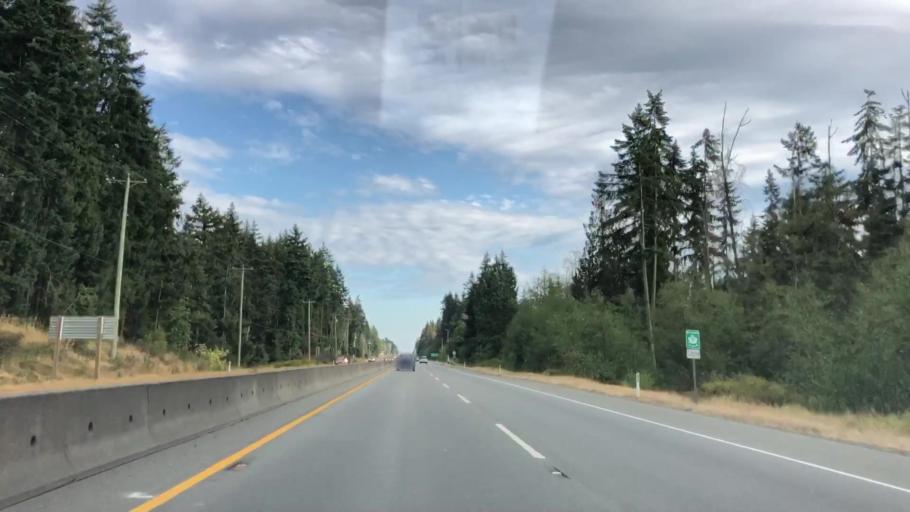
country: CA
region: British Columbia
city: Duncan
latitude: 48.7044
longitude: -123.6034
